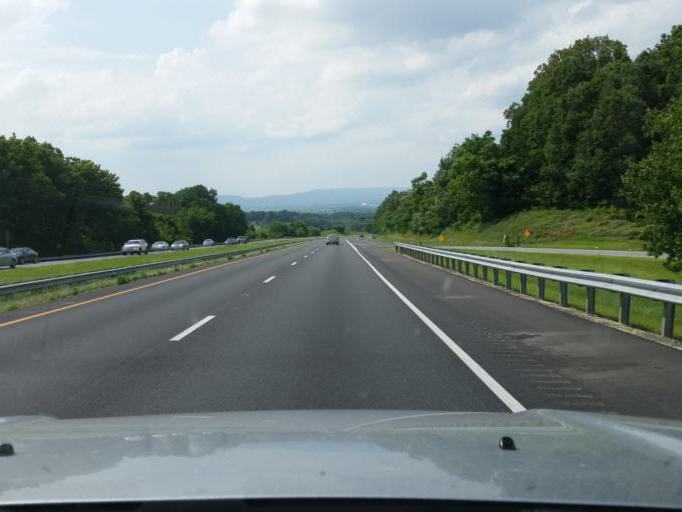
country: US
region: Maryland
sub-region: Frederick County
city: Buckeystown
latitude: 39.3475
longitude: -77.3899
